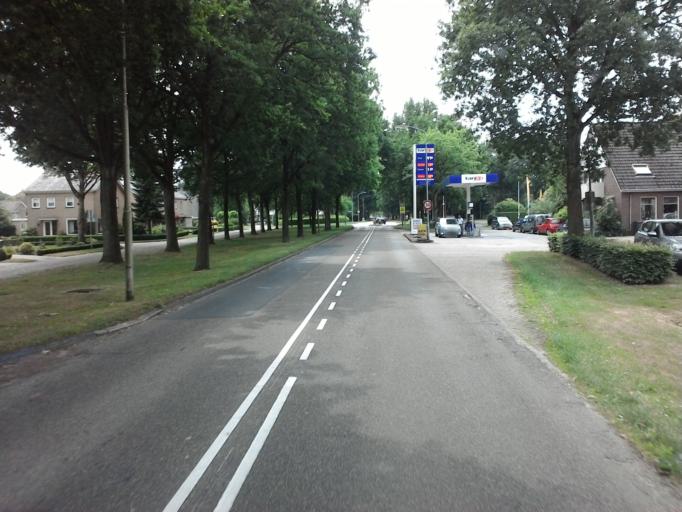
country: NL
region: Drenthe
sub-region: Gemeente Aa en Hunze
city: Anloo
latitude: 52.9829
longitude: 6.6490
